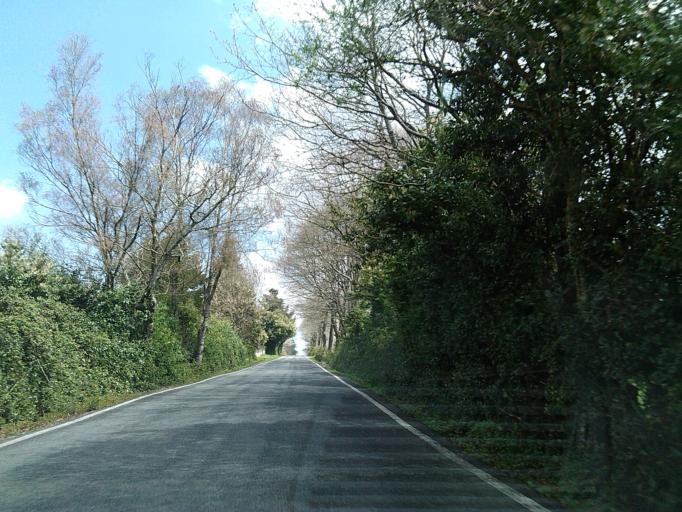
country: ES
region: Galicia
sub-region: Provincia da Coruna
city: Sobrado
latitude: 43.0323
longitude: -7.9320
